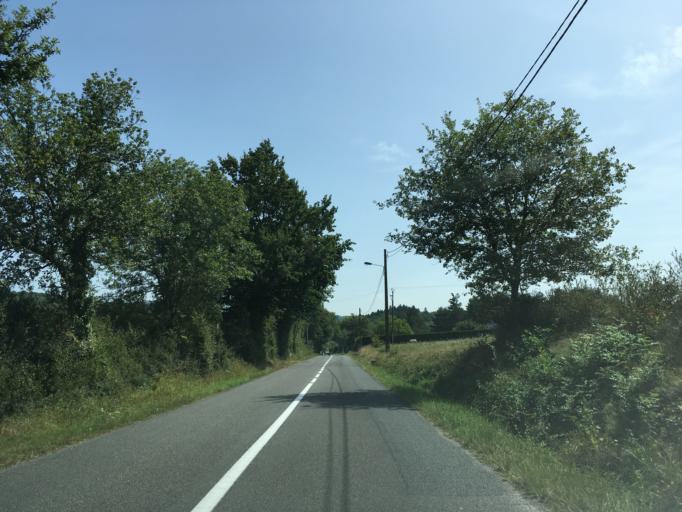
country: FR
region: Midi-Pyrenees
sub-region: Departement du Tarn
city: Burlats
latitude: 43.6207
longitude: 2.2875
